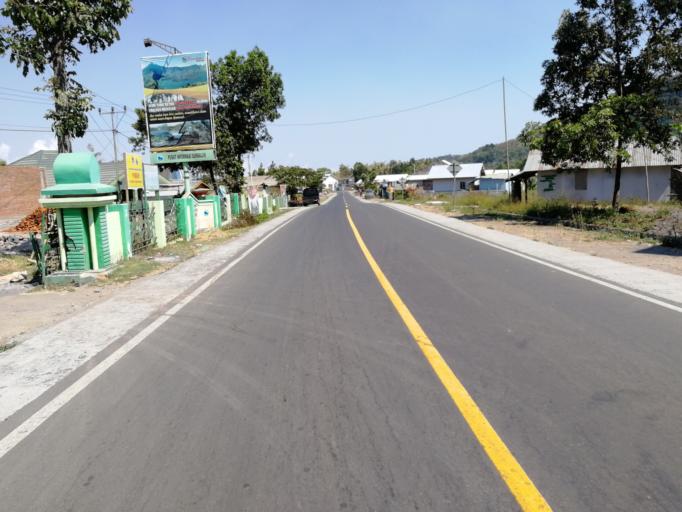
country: ID
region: West Nusa Tenggara
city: Sembalunlawang
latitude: -8.3598
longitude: 116.5246
